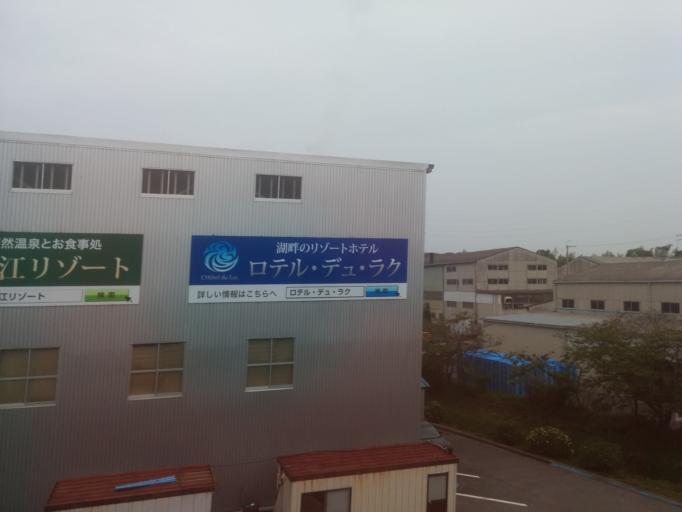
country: JP
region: Shiga Prefecture
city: Youkaichi
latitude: 35.1907
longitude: 136.1782
